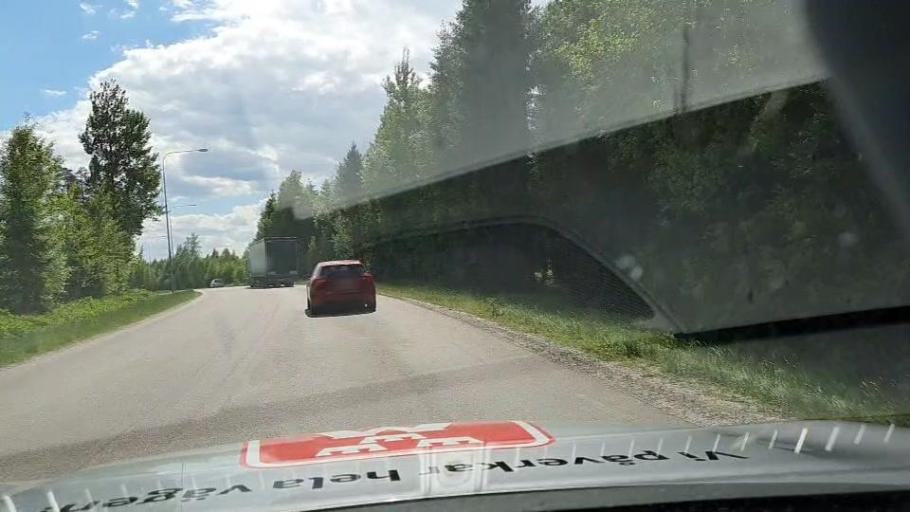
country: SE
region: Kronoberg
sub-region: Ljungby Kommun
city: Ljungby
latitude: 56.8544
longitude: 13.9308
